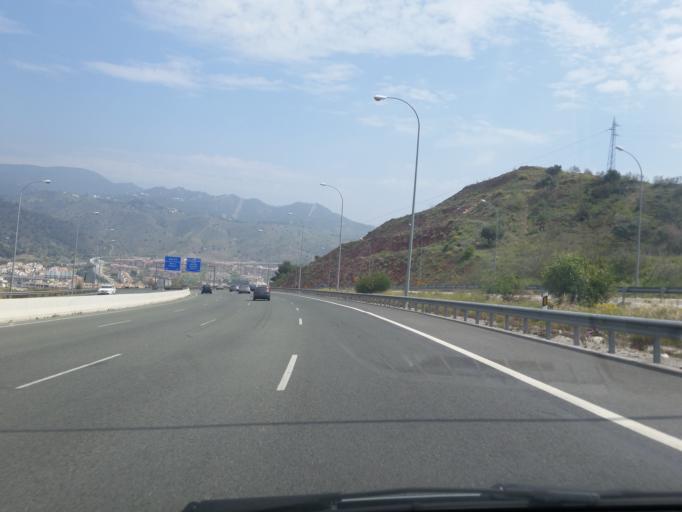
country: ES
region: Andalusia
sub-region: Provincia de Malaga
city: Malaga
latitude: 36.7472
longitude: -4.4368
